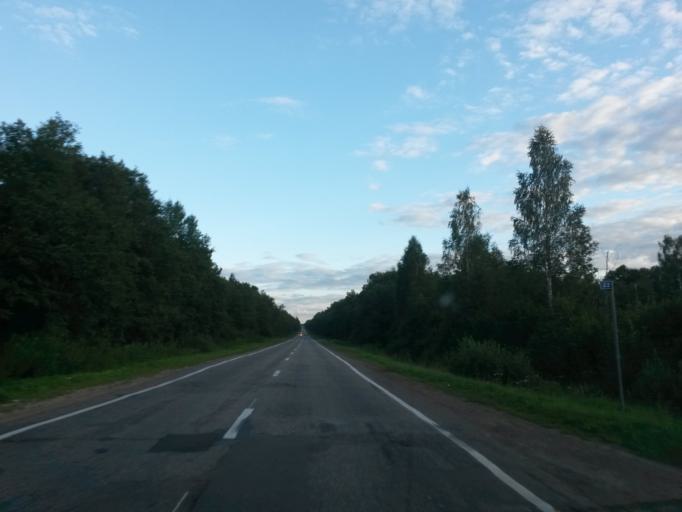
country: RU
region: Jaroslavl
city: Gavrilov-Yam
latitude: 57.4375
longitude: 39.9176
